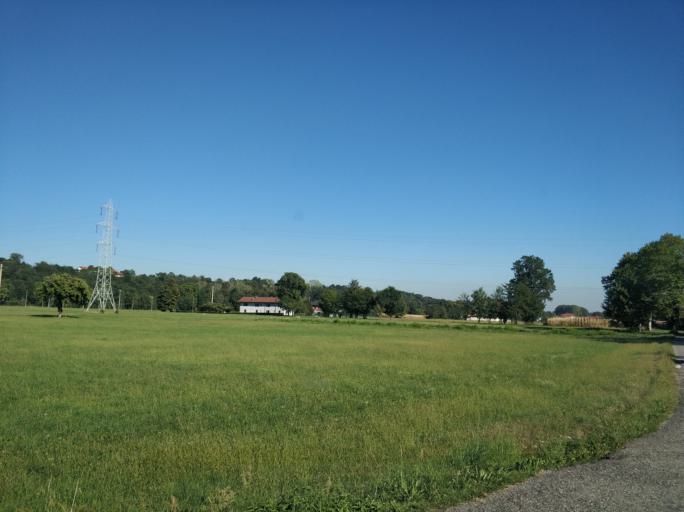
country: IT
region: Piedmont
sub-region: Provincia di Torino
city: Grosso
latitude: 45.2610
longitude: 7.5499
